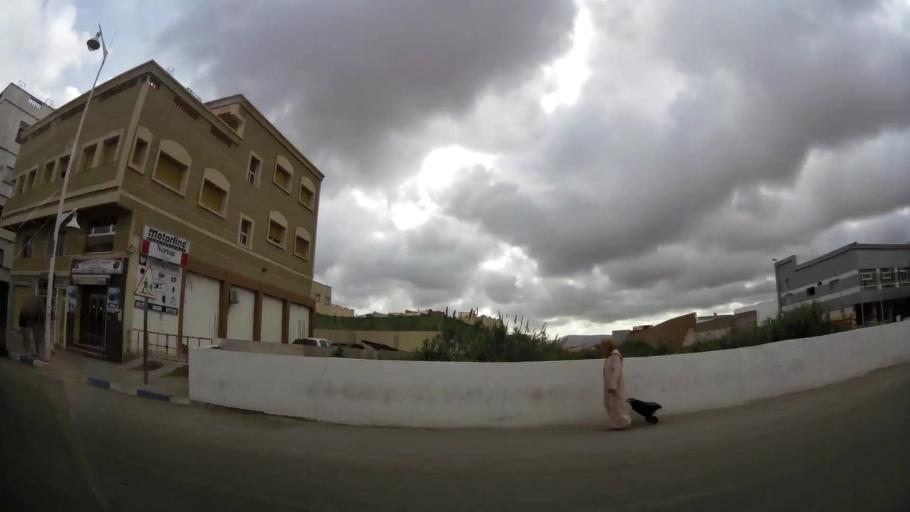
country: MA
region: Oriental
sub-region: Nador
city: Nador
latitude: 35.1576
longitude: -2.9301
